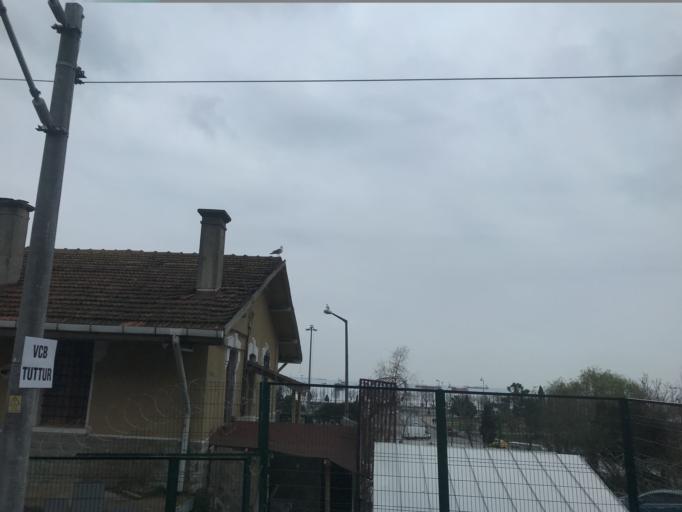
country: TR
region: Istanbul
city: Adalar
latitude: 40.8877
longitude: 29.1835
